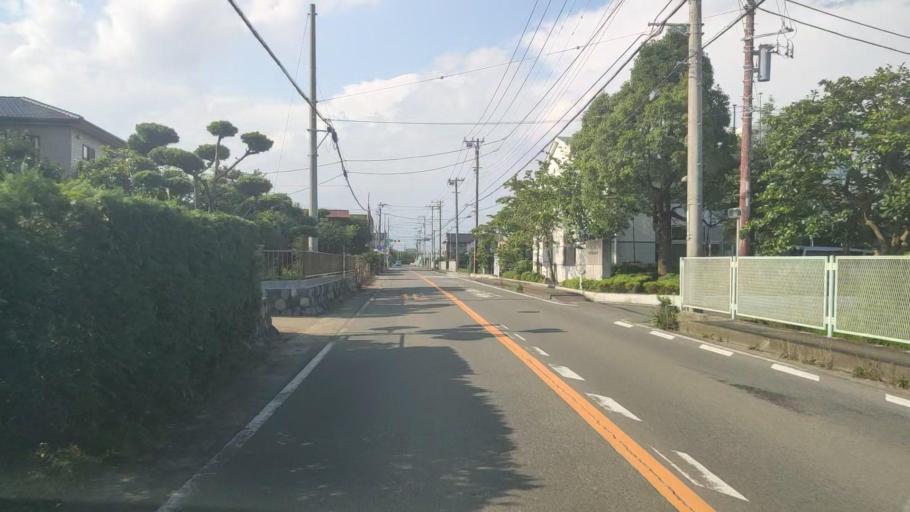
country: JP
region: Kanagawa
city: Isehara
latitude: 35.3726
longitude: 139.3325
